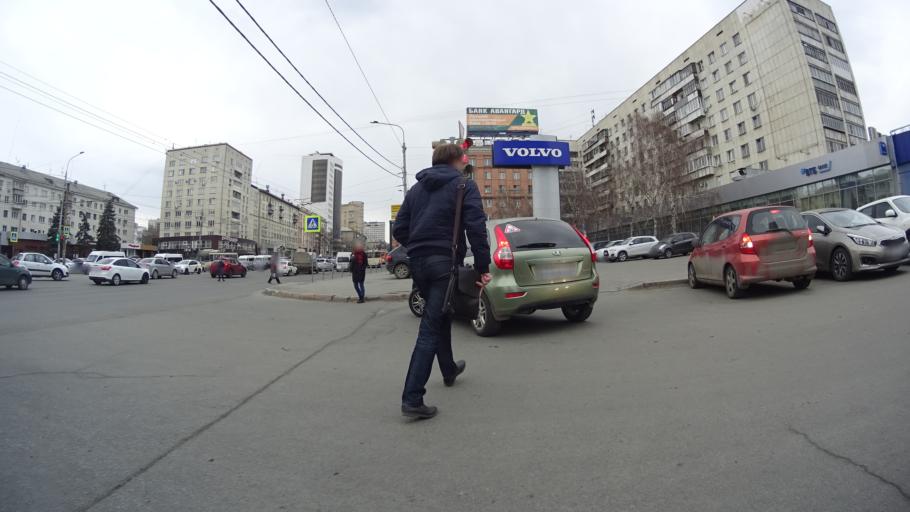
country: RU
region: Chelyabinsk
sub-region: Gorod Chelyabinsk
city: Chelyabinsk
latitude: 55.1611
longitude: 61.4256
